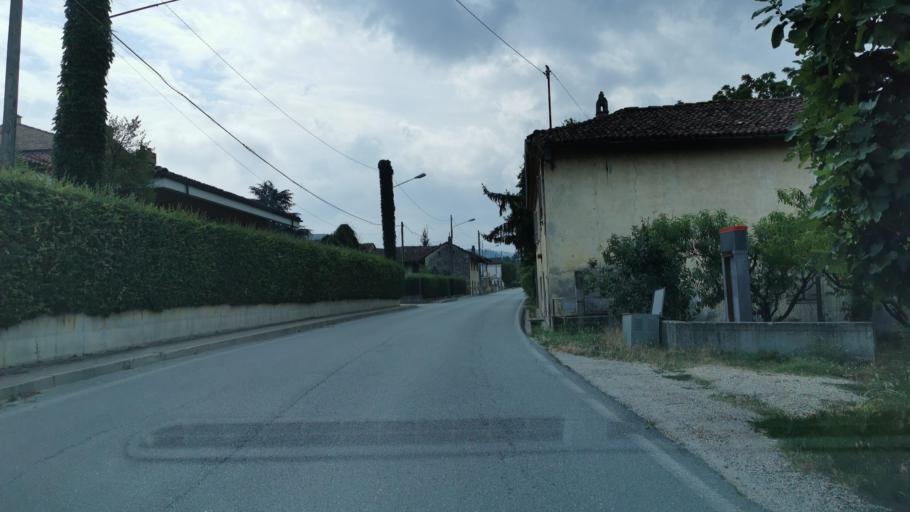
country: IT
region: Piedmont
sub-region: Provincia di Cuneo
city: Grinzane Cavour
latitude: 44.6450
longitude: 7.9984
